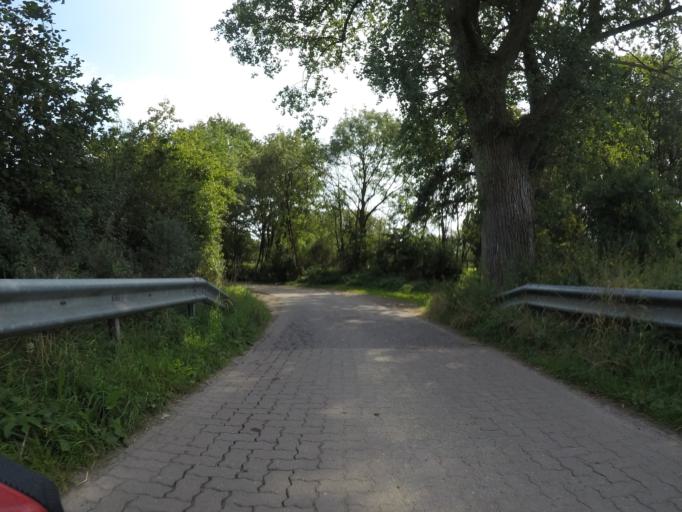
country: DE
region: Schleswig-Holstein
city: Kisdorf
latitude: 53.7971
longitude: 10.0235
